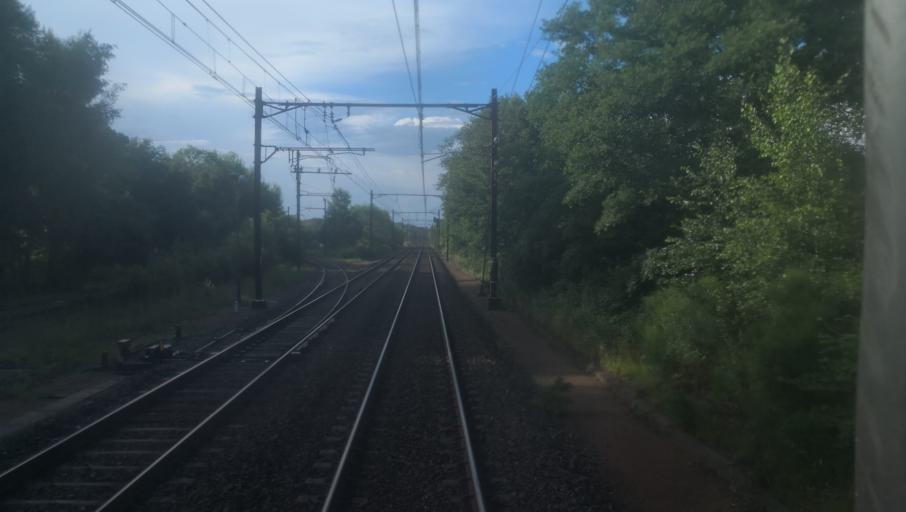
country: FR
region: Centre
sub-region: Departement du Loir-et-Cher
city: Salbris
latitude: 47.4377
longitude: 2.0450
